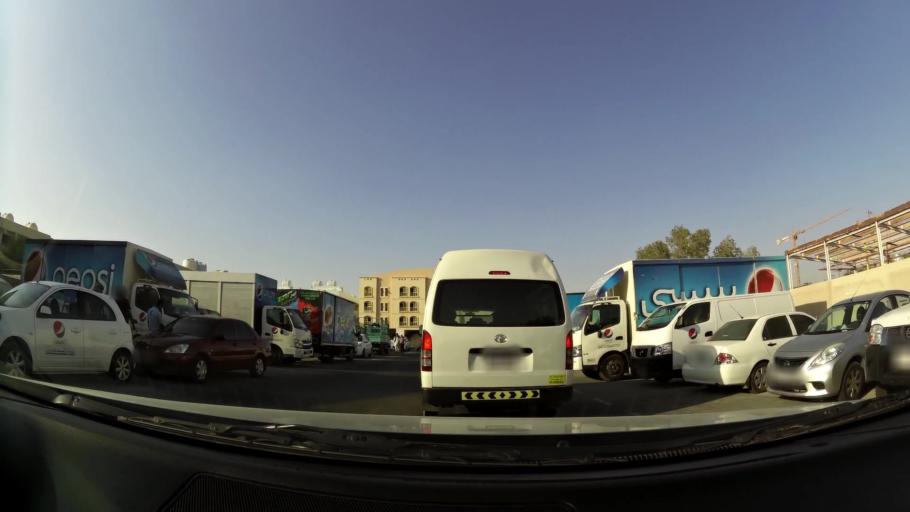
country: AE
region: Dubai
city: Dubai
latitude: 25.1300
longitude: 55.2354
